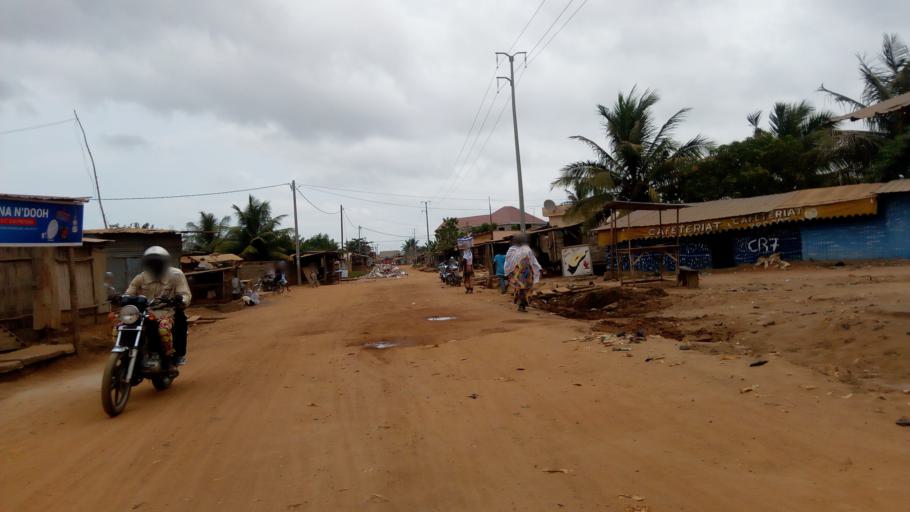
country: TG
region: Maritime
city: Lome
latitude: 6.2549
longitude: 1.2177
